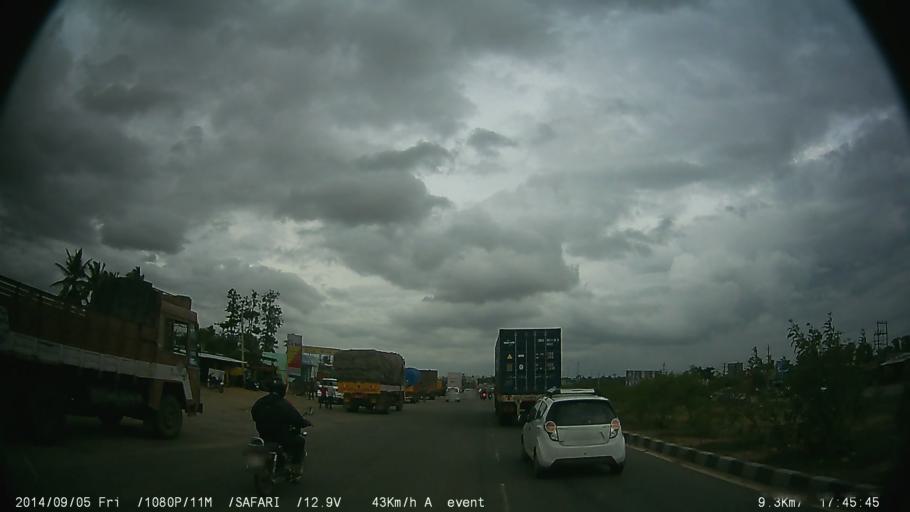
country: IN
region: Tamil Nadu
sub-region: Krishnagiri
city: Hosur
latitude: 12.7756
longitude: 77.7792
